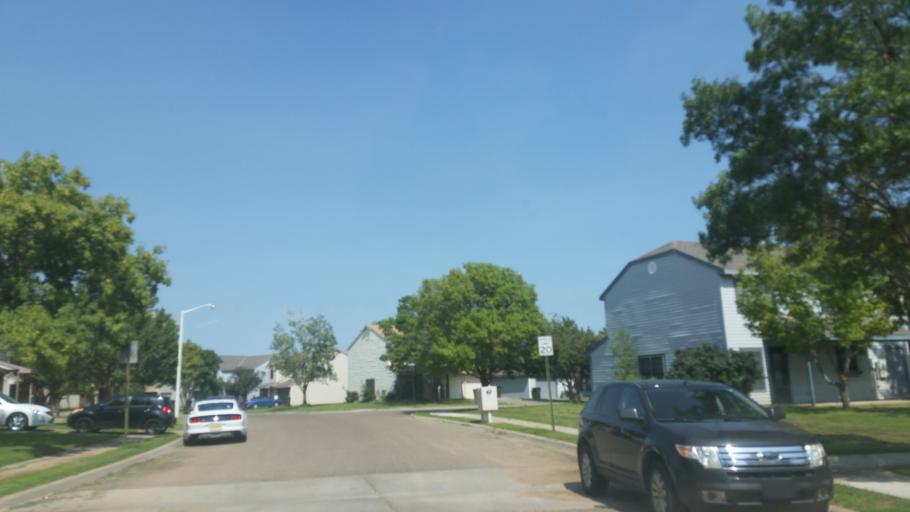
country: US
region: New Mexico
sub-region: Curry County
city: Clovis
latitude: 34.4452
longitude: -103.1742
